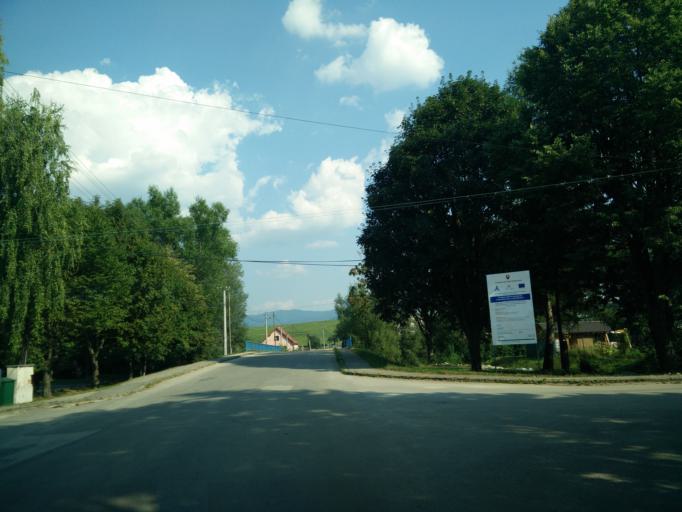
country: SK
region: Zilinsky
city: Rajec
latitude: 49.1193
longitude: 18.6509
